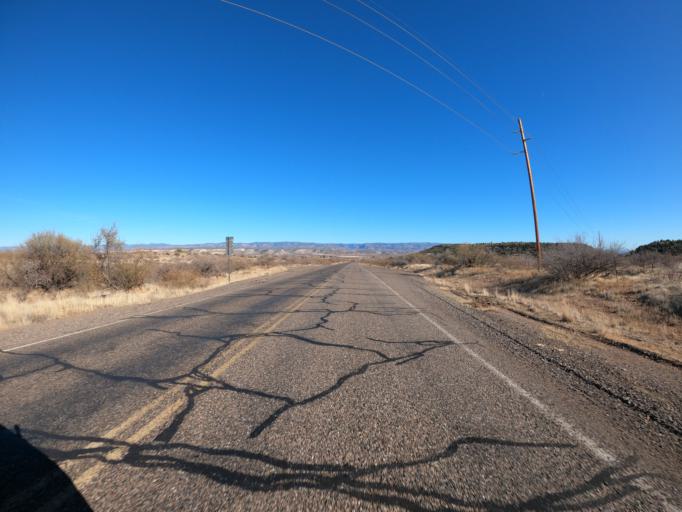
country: US
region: Arizona
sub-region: Yavapai County
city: Camp Verde
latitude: 34.5580
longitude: -111.8935
